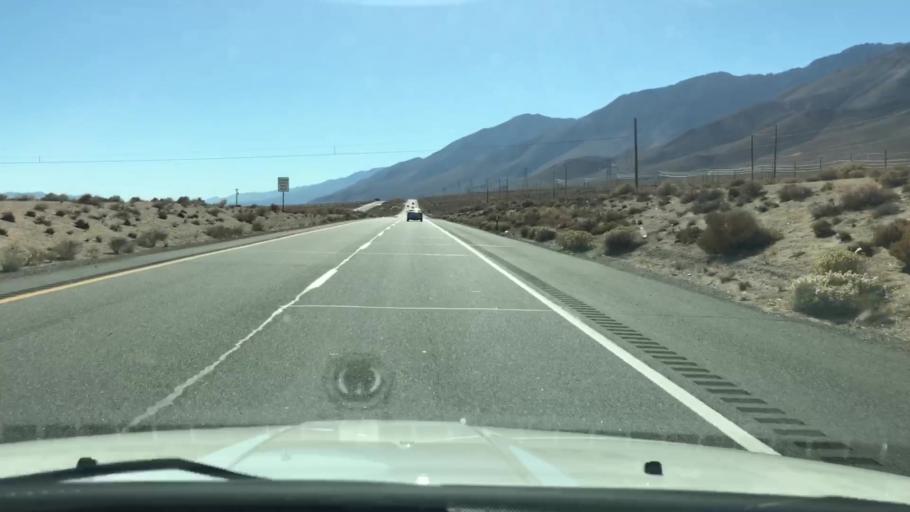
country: US
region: California
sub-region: Inyo County
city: Lone Pine
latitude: 36.4906
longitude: -118.0342
